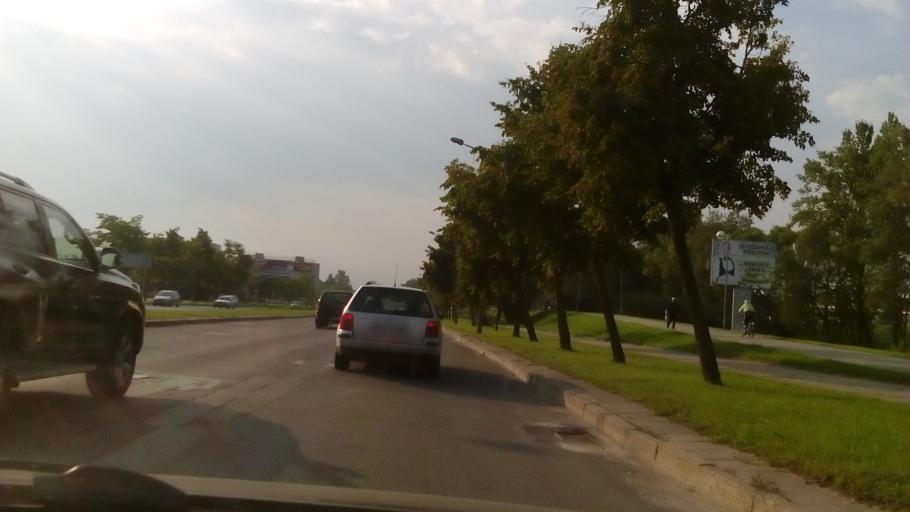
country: LT
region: Alytaus apskritis
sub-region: Alytus
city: Alytus
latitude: 54.4043
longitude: 24.0204
